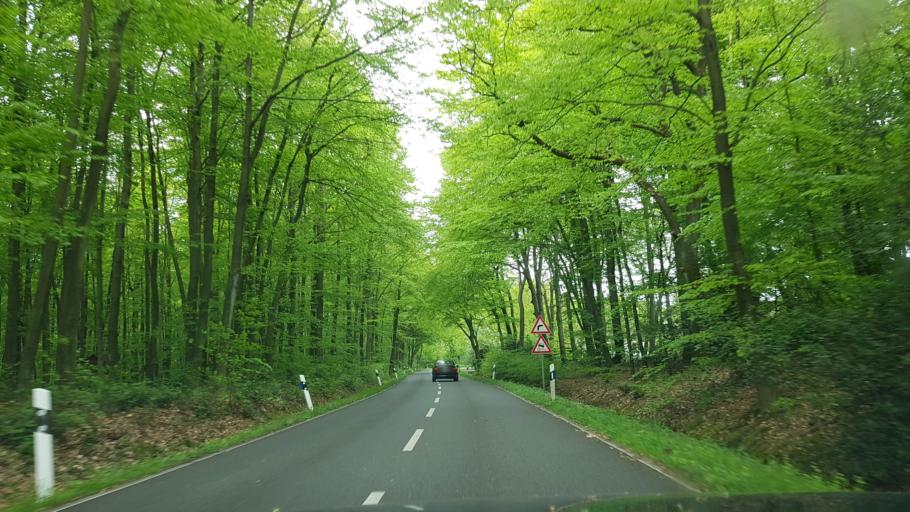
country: DE
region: North Rhine-Westphalia
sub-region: Regierungsbezirk Dusseldorf
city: Muelheim (Ruhr)
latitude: 51.4002
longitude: 6.8414
